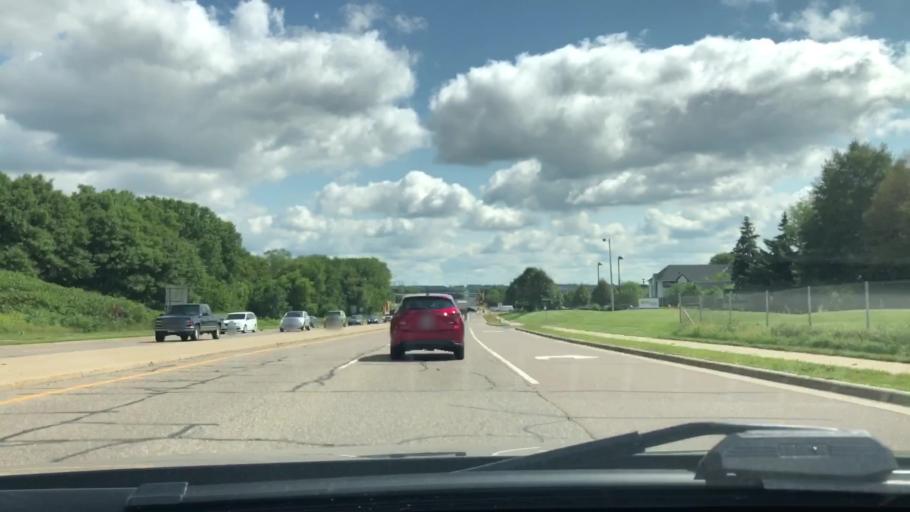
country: US
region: Minnesota
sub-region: Dakota County
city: Mendota Heights
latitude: 44.8479
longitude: -93.1503
